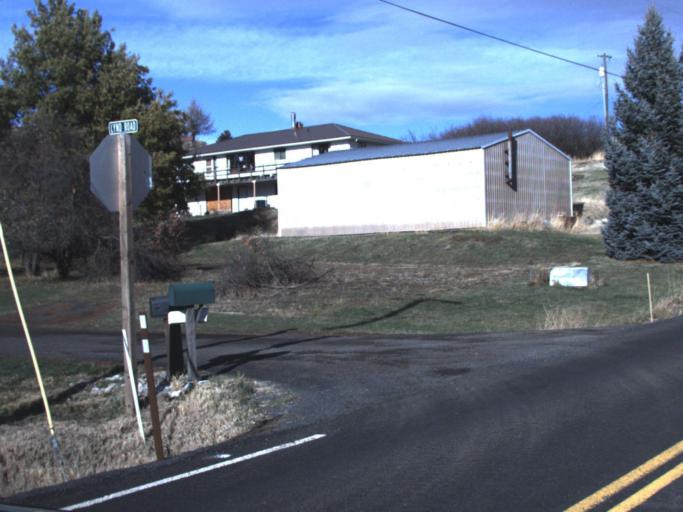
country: US
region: Idaho
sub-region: Latah County
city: Moscow
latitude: 46.9155
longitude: -117.0663
